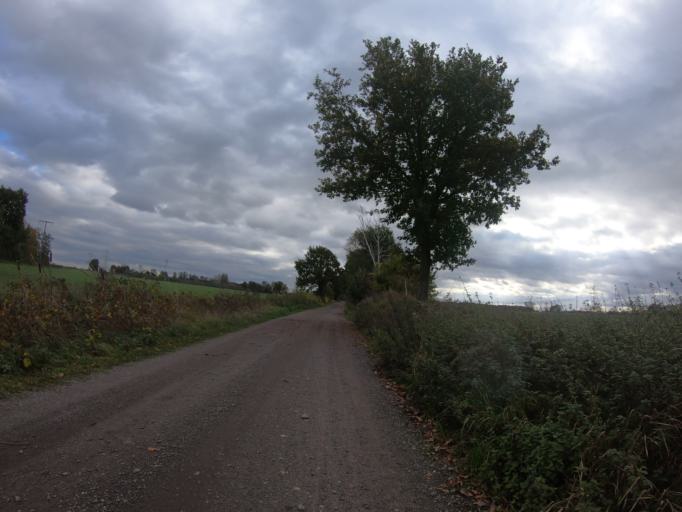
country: DE
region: Lower Saxony
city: Vordorf
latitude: 52.3740
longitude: 10.5015
